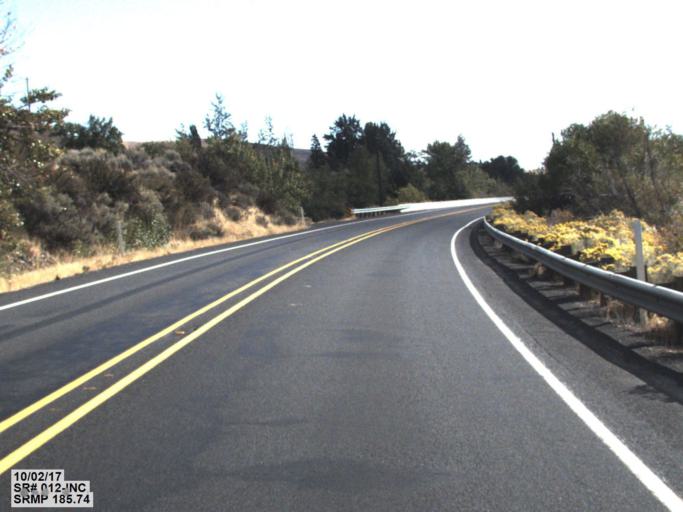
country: US
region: Washington
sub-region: Yakima County
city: Tieton
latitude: 46.7488
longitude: -120.7816
